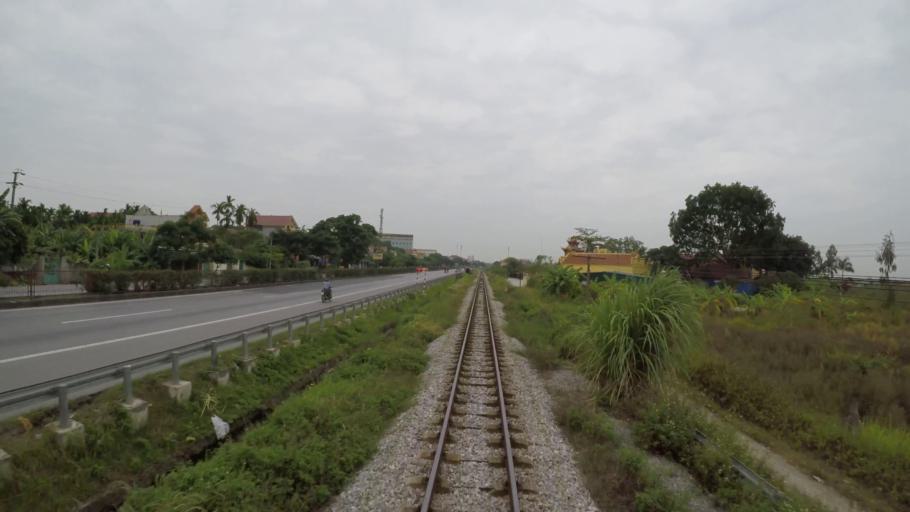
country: VN
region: Hai Duong
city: Phu Thai
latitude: 20.9446
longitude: 106.5424
